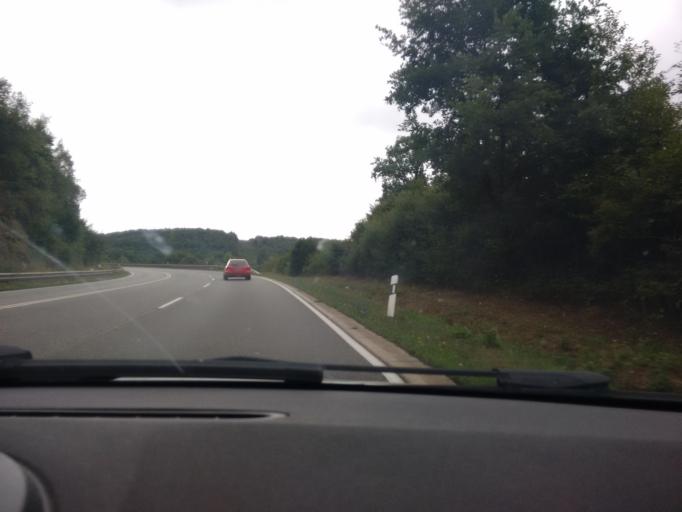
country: DE
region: Rheinland-Pfalz
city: Idar-Oberstein
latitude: 49.6991
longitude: 7.3114
